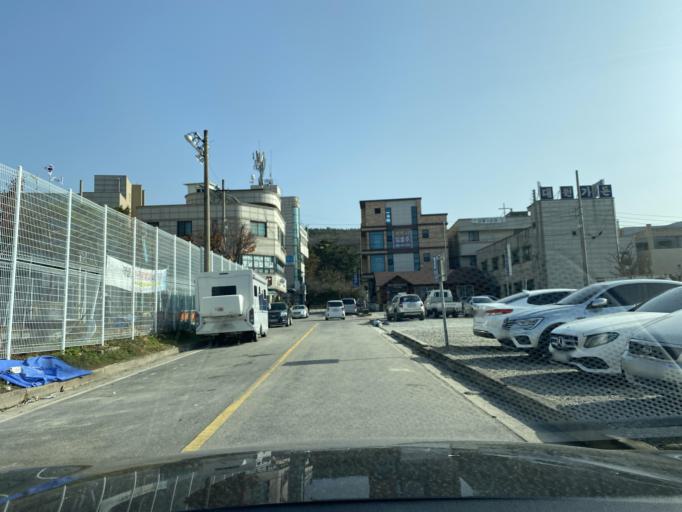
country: KR
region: Chungcheongnam-do
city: Yesan
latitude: 36.6941
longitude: 126.8352
